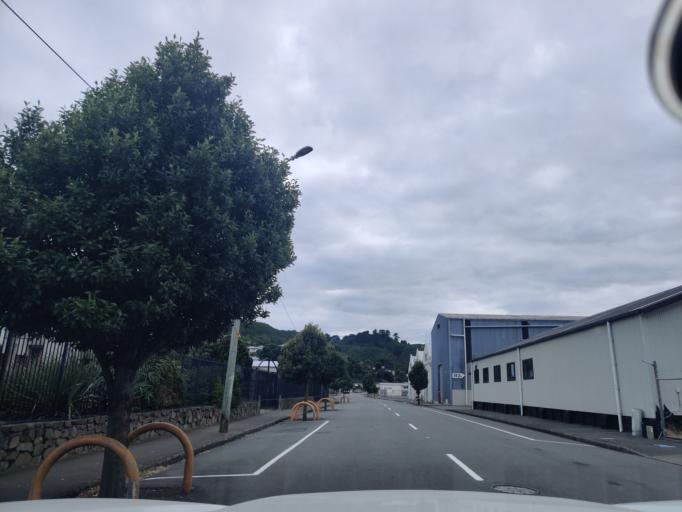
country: NZ
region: Wellington
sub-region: Wellington City
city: Wellington
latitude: -41.3090
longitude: 174.8215
